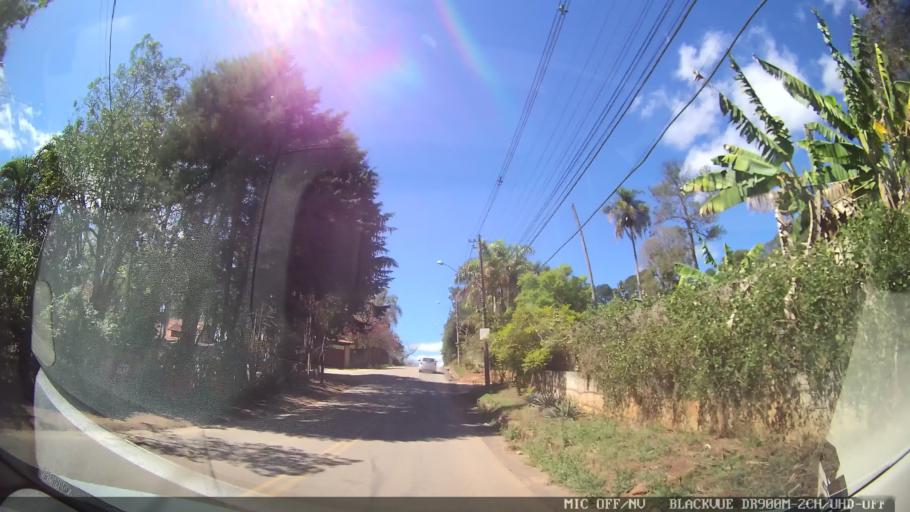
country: BR
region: Sao Paulo
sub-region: Campo Limpo Paulista
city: Campo Limpo Paulista
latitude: -23.1789
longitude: -46.7594
